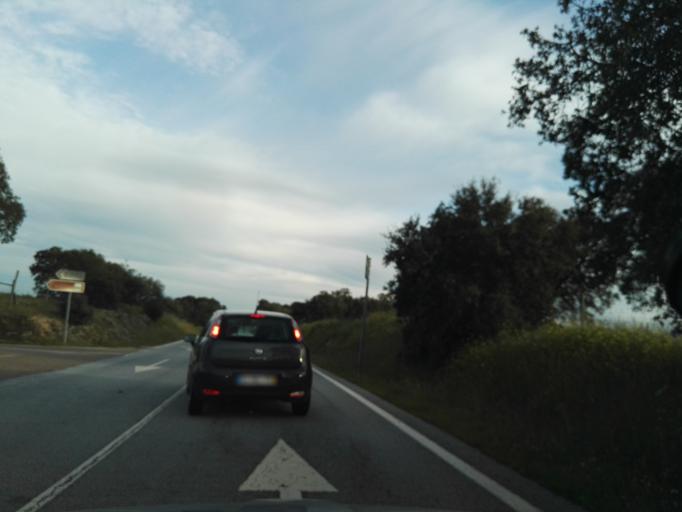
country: PT
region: Portalegre
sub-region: Arronches
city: Arronches
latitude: 39.0653
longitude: -7.2757
